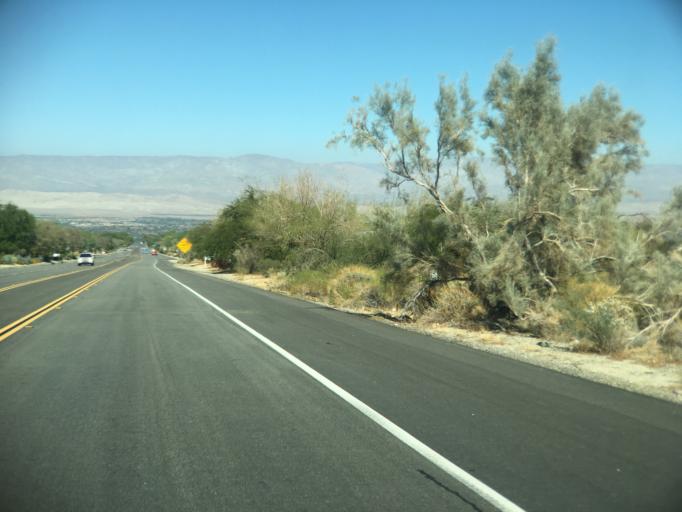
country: US
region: California
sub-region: Riverside County
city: Palm Desert
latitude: 33.6735
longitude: -116.4089
